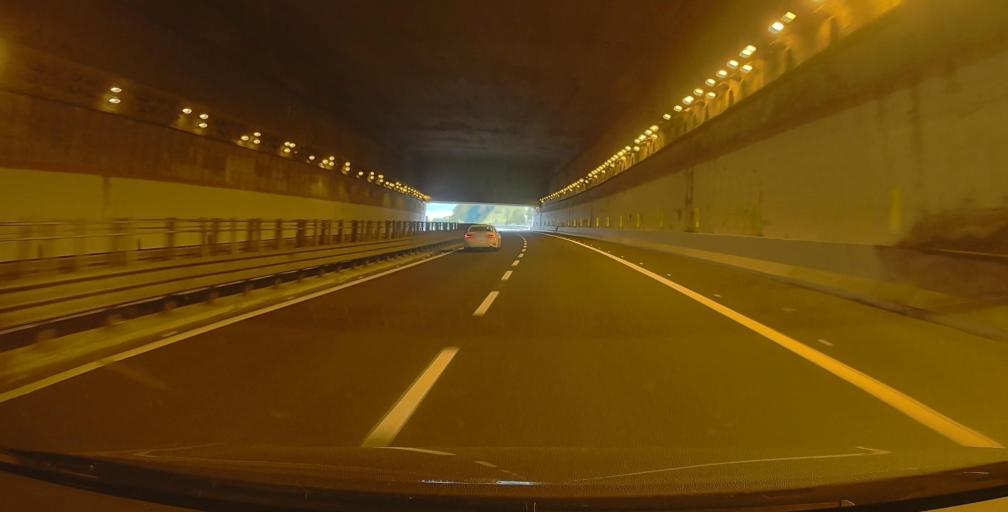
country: IT
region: Calabria
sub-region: Provincia di Vibo-Valentia
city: Paravati
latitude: 38.5719
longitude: 16.0913
